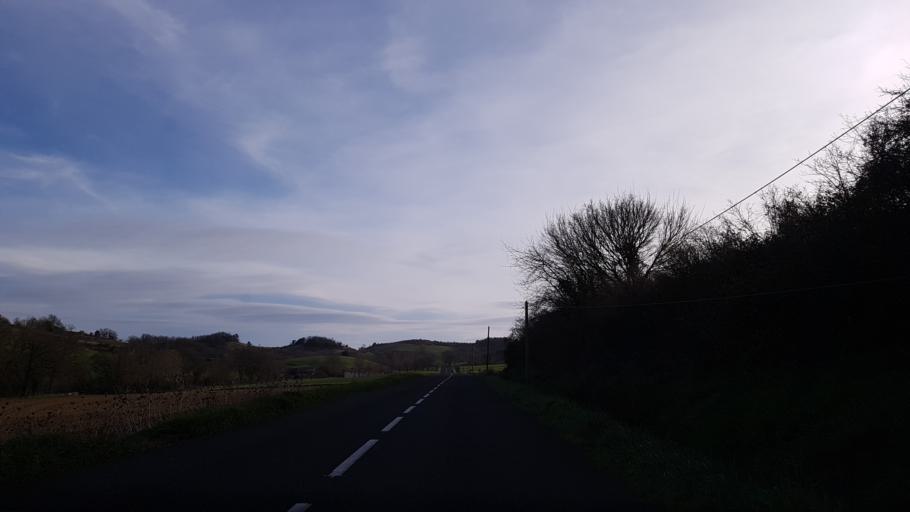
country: FR
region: Midi-Pyrenees
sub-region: Departement de l'Ariege
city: Mirepoix
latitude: 43.1424
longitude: 1.9128
